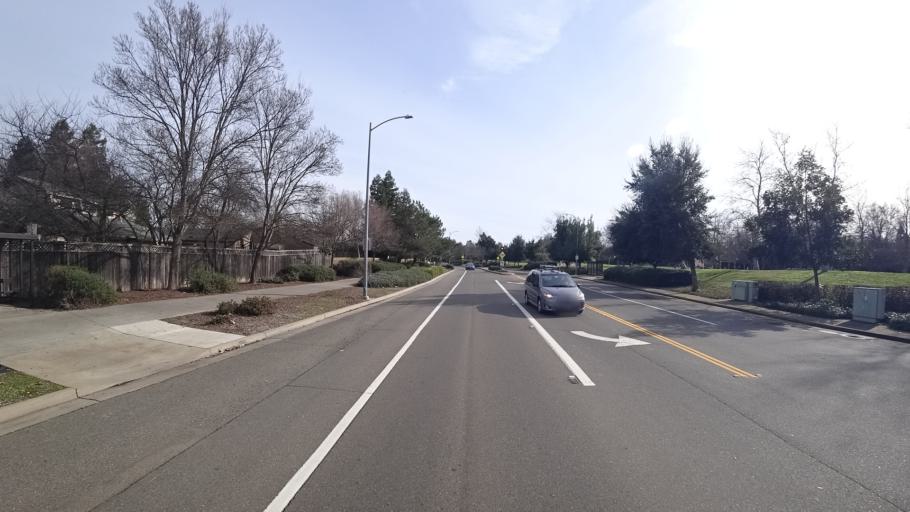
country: US
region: California
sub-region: Yolo County
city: Davis
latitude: 38.5476
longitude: -121.7065
